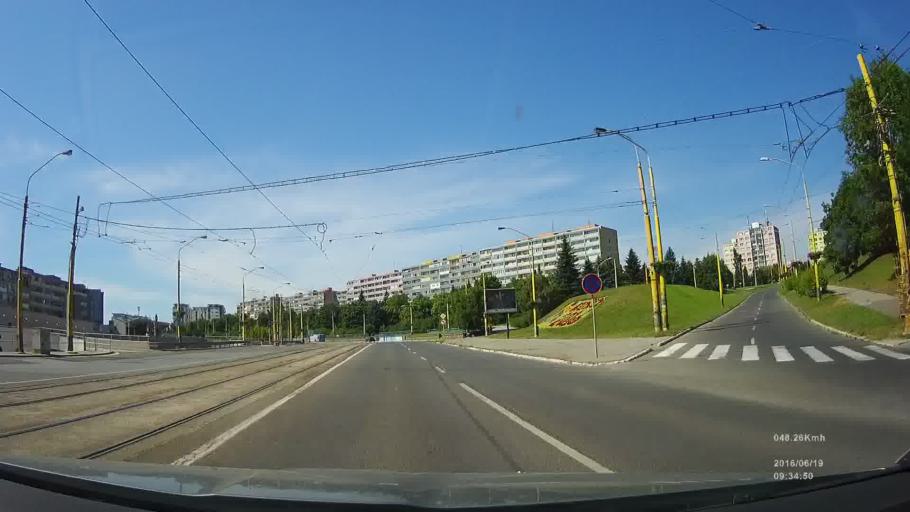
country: SK
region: Kosicky
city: Kosice
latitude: 48.7150
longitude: 21.2472
